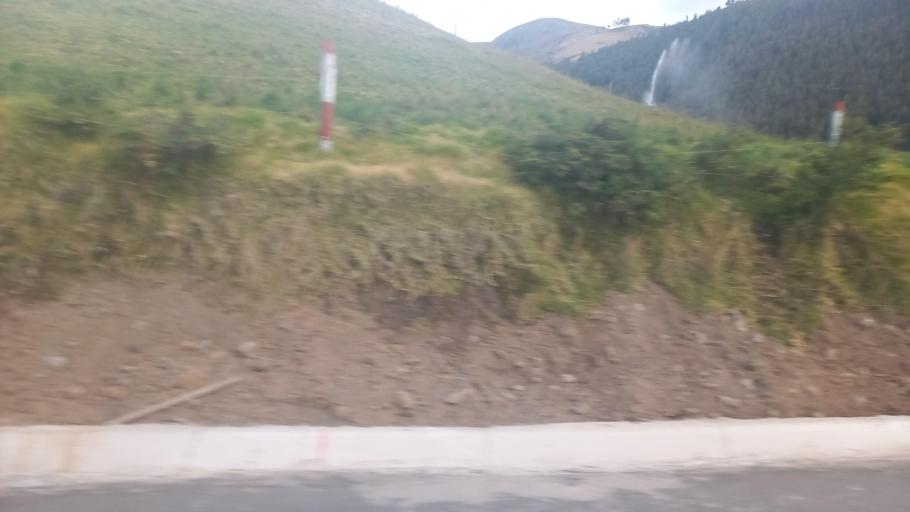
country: EC
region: Pichincha
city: Cayambe
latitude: 0.1288
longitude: -78.0696
